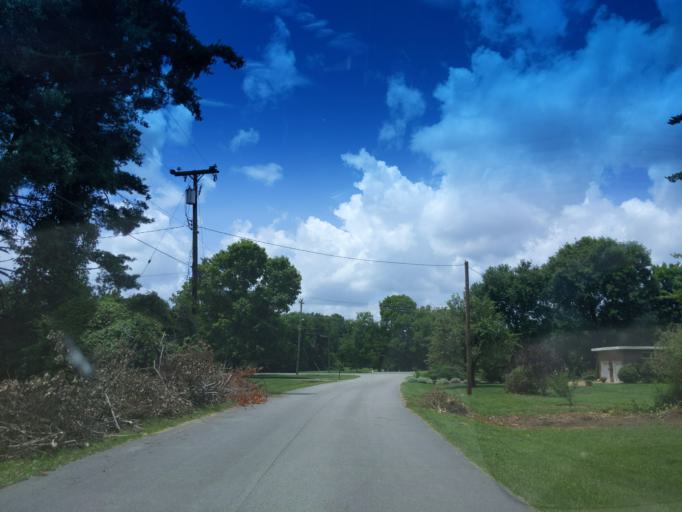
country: US
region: Tennessee
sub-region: Williamson County
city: Brentwood Estates
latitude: 36.0132
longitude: -86.7800
